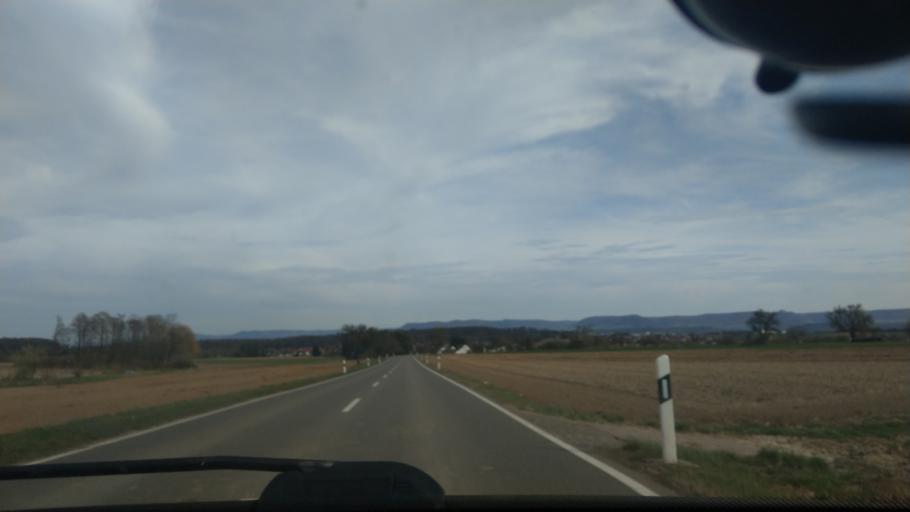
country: DE
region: Baden-Wuerttemberg
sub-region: Regierungsbezirk Stuttgart
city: Wolfschlugen
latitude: 48.6623
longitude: 9.2758
